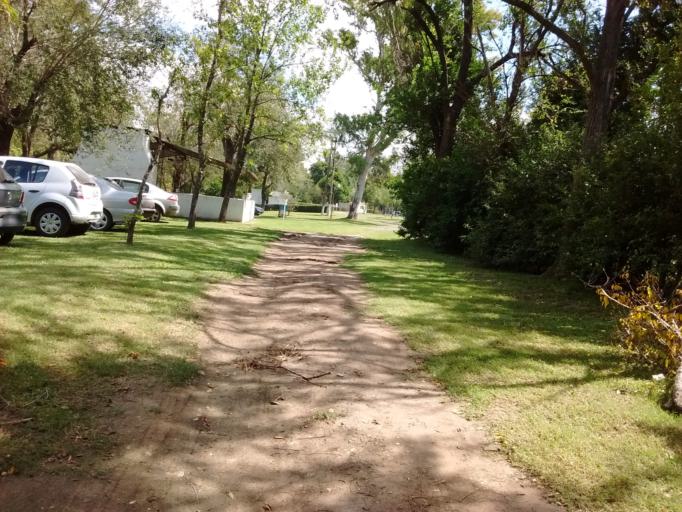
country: AR
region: Santa Fe
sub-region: Departamento de San Lorenzo
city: San Lorenzo
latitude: -32.6386
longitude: -60.8169
